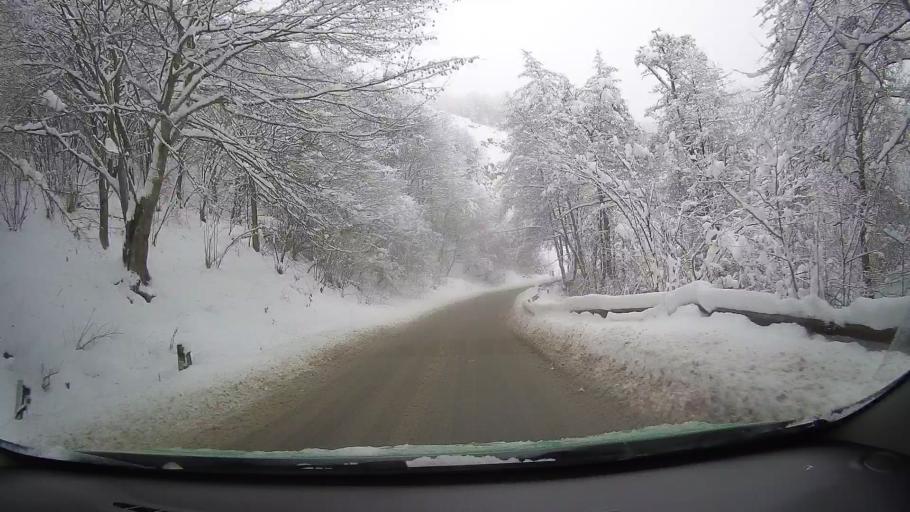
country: RO
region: Sibiu
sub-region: Comuna Tilisca
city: Tilisca
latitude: 45.8017
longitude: 23.8098
